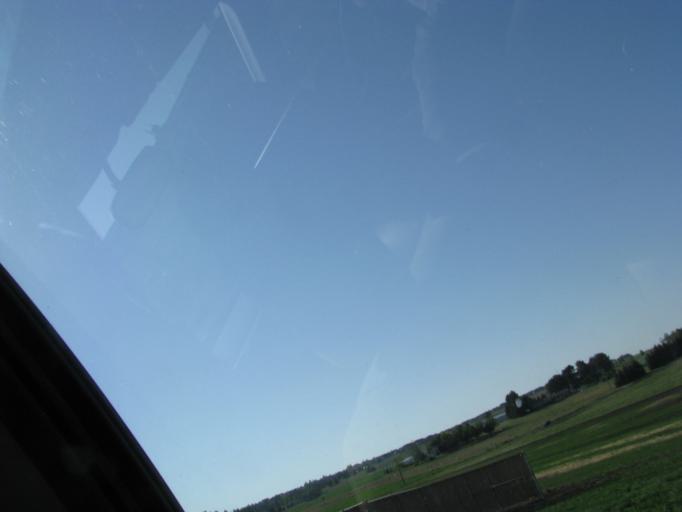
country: US
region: Washington
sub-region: Spokane County
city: Liberty Lake
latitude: 47.6278
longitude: -117.1509
